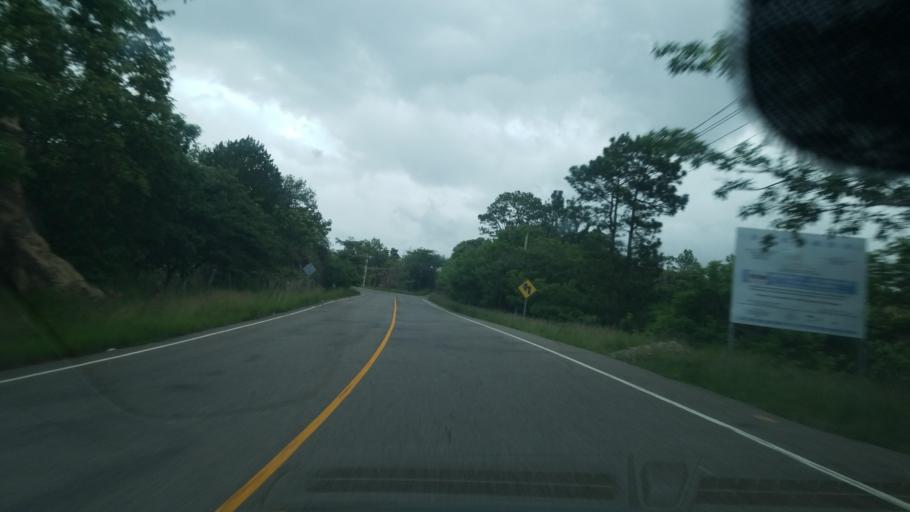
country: HN
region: Ocotepeque
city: Sinuapa
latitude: 14.5223
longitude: -89.2456
